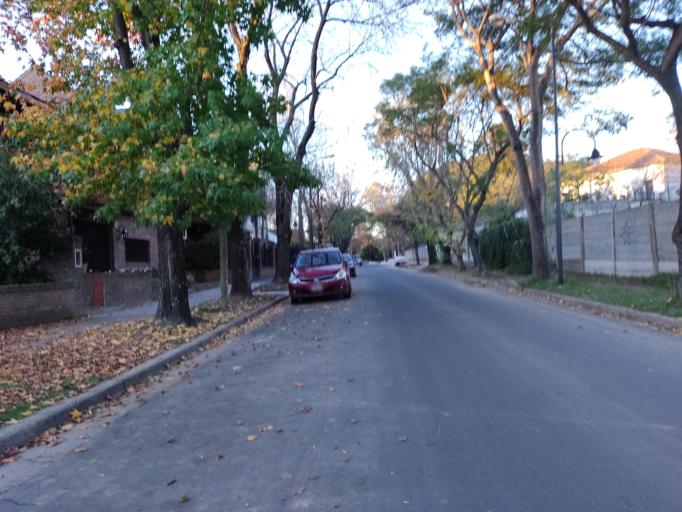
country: AR
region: Buenos Aires
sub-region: Partido de San Isidro
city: San Isidro
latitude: -34.4491
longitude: -58.5386
